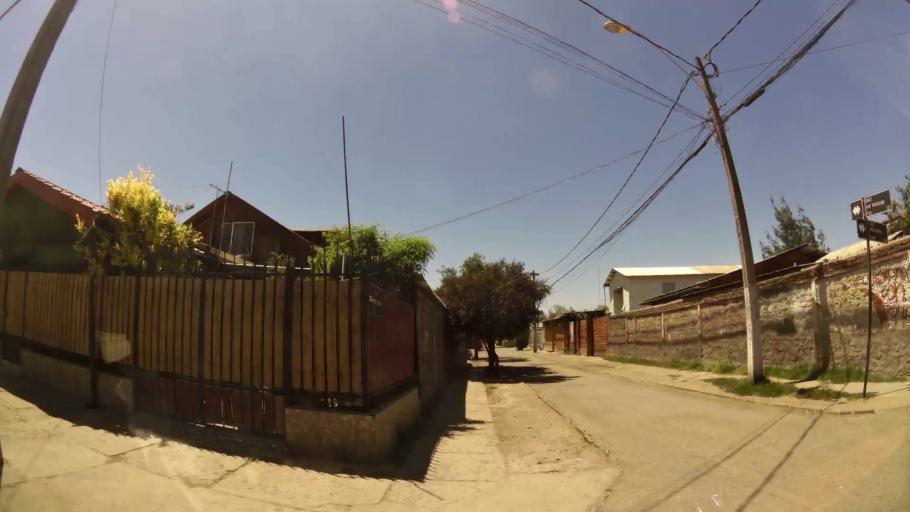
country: CL
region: Santiago Metropolitan
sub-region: Provincia de Santiago
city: La Pintana
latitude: -33.5684
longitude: -70.6682
